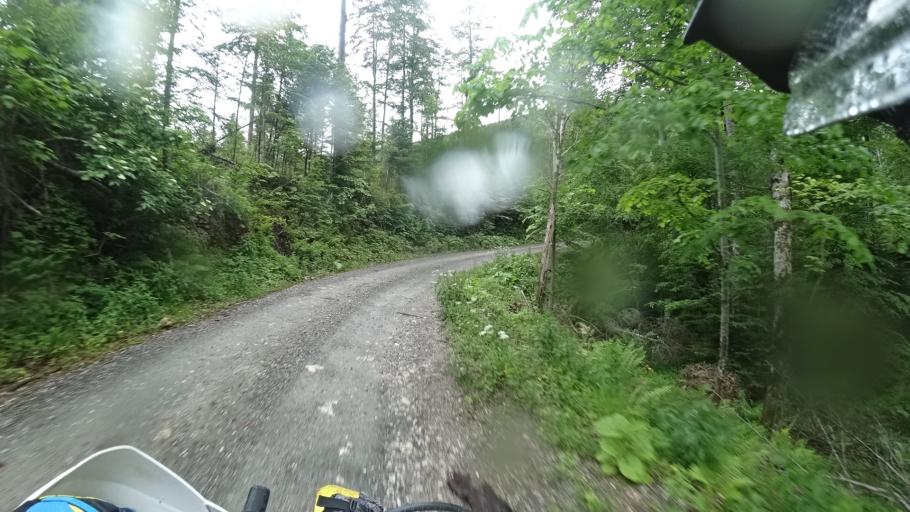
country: HR
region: Primorsko-Goranska
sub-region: Grad Delnice
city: Delnice
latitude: 45.3225
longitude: 14.9294
